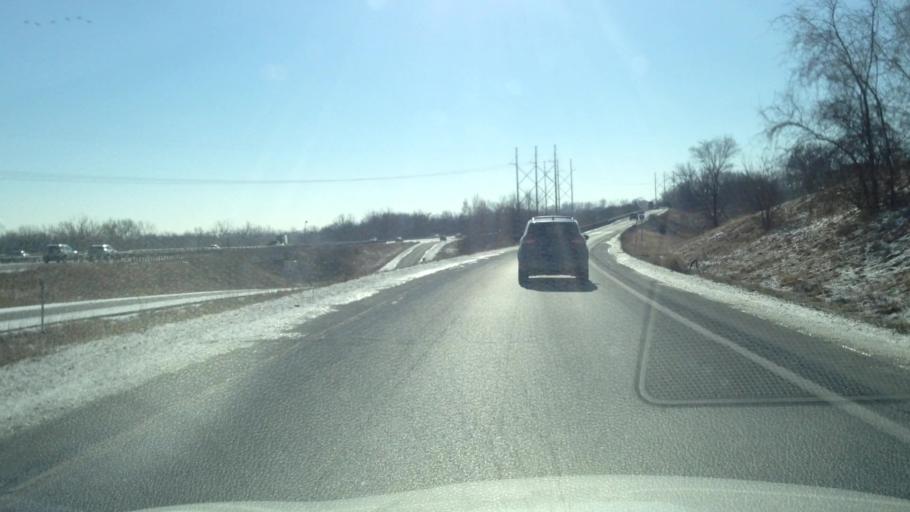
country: US
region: Missouri
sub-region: Clay County
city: Gladstone
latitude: 39.1751
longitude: -94.5613
